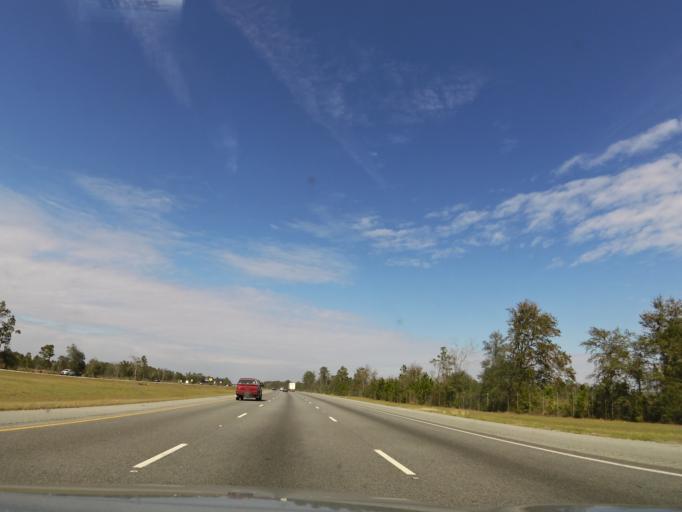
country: US
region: Georgia
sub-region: McIntosh County
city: Darien
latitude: 31.4193
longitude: -81.4431
